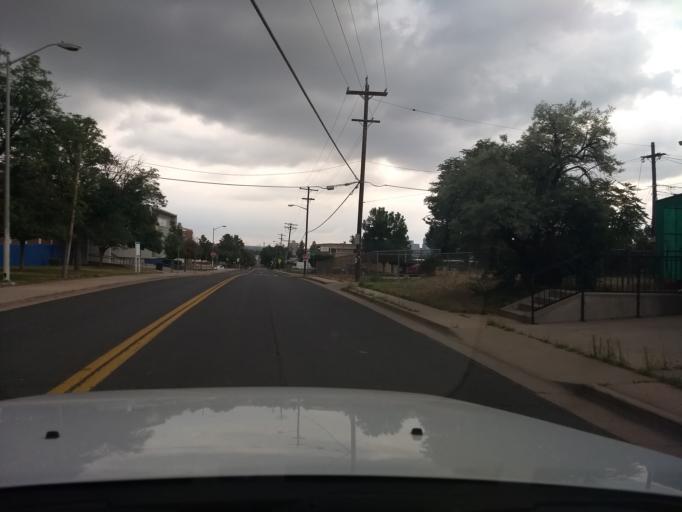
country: US
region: Colorado
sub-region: Denver County
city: Denver
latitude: 39.7078
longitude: -105.0110
